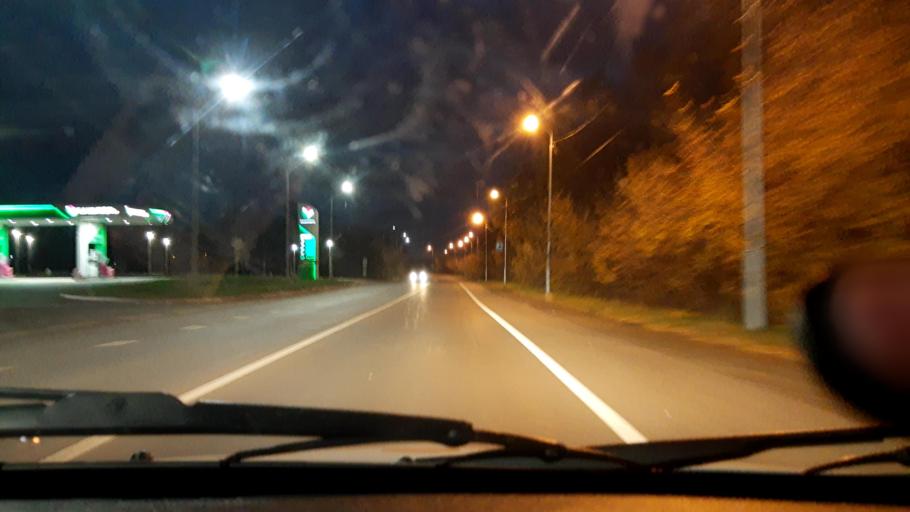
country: RU
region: Bashkortostan
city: Blagoveshchensk
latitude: 54.9059
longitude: 56.0566
